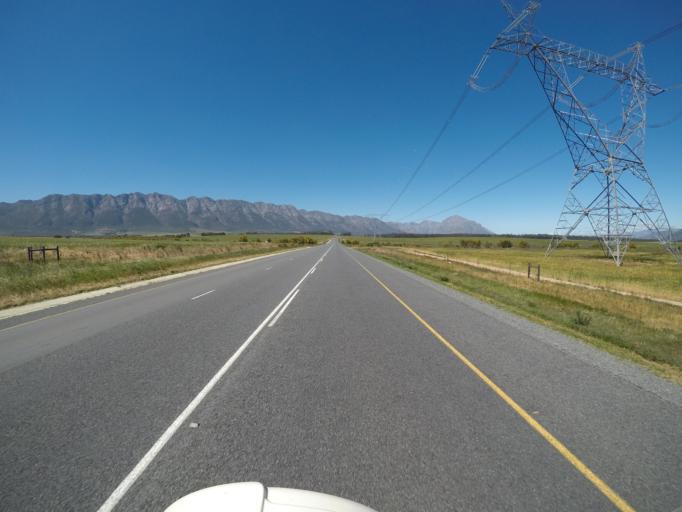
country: ZA
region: Western Cape
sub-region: Cape Winelands District Municipality
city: Ceres
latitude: -33.3230
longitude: 19.1447
